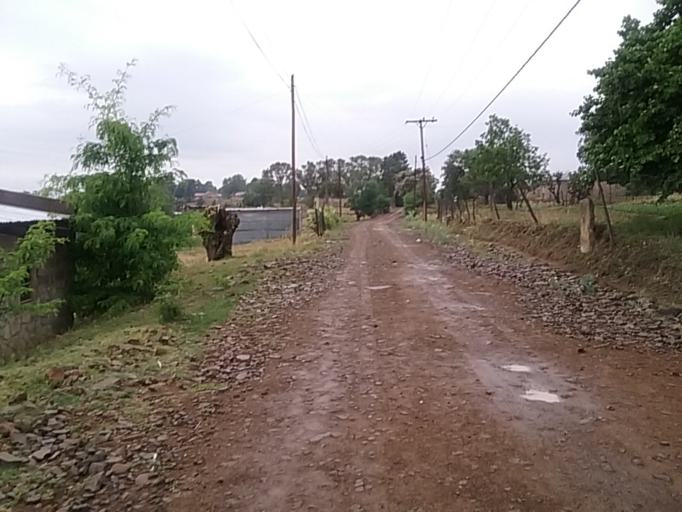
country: LS
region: Berea
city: Teyateyaneng
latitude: -29.1398
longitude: 27.7378
